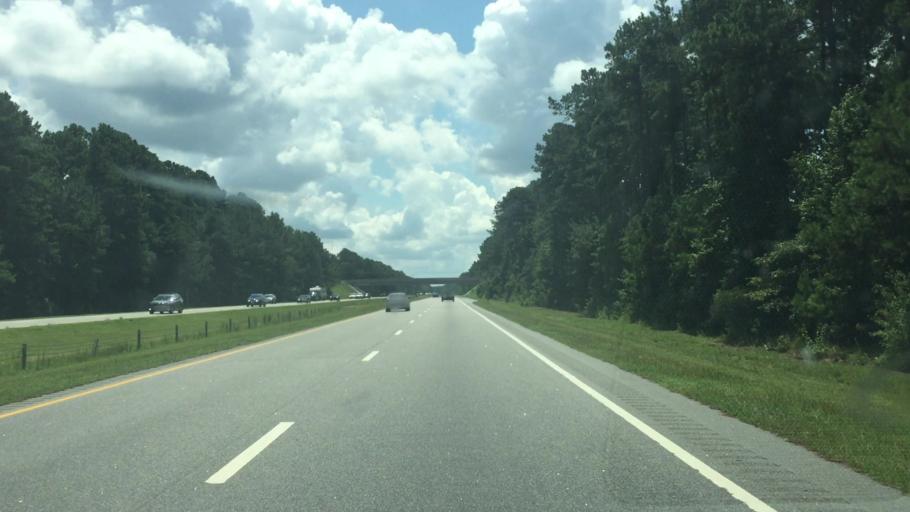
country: US
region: North Carolina
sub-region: Robeson County
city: Lumberton
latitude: 34.5481
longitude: -79.0227
